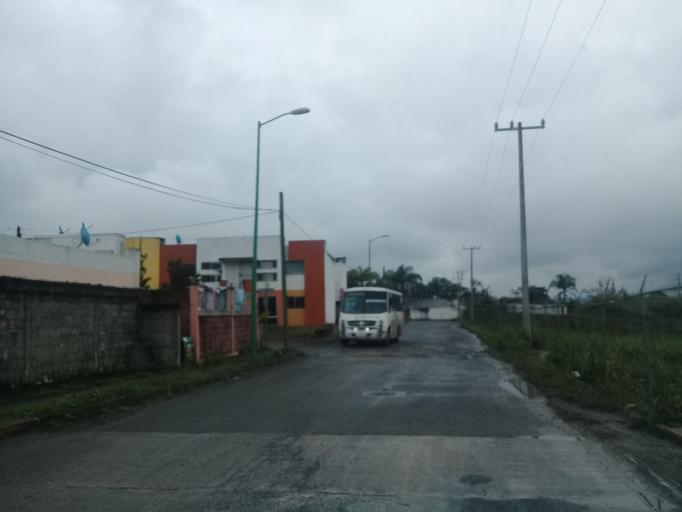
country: MX
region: Veracruz
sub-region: Amatlan de los Reyes
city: Trapiche Viejo
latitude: 18.8368
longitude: -96.9515
